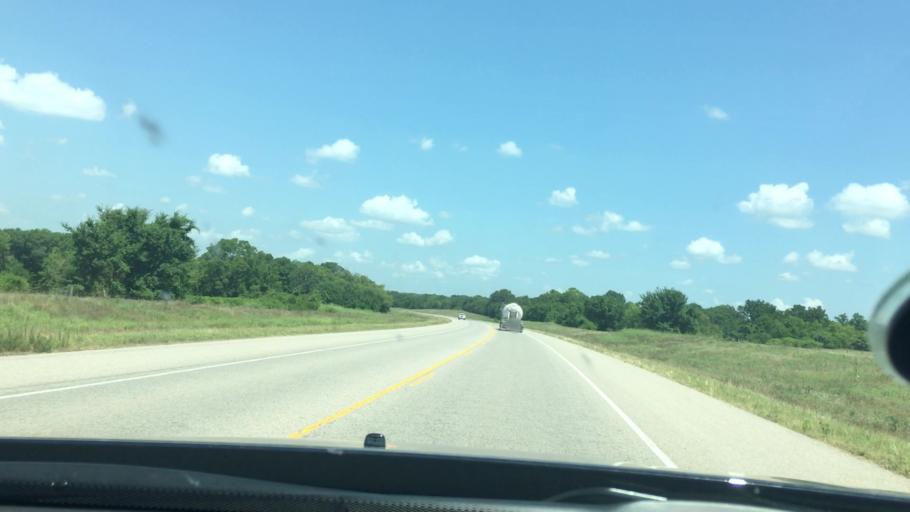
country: US
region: Oklahoma
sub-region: Pontotoc County
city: Ada
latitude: 34.6951
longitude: -96.5976
